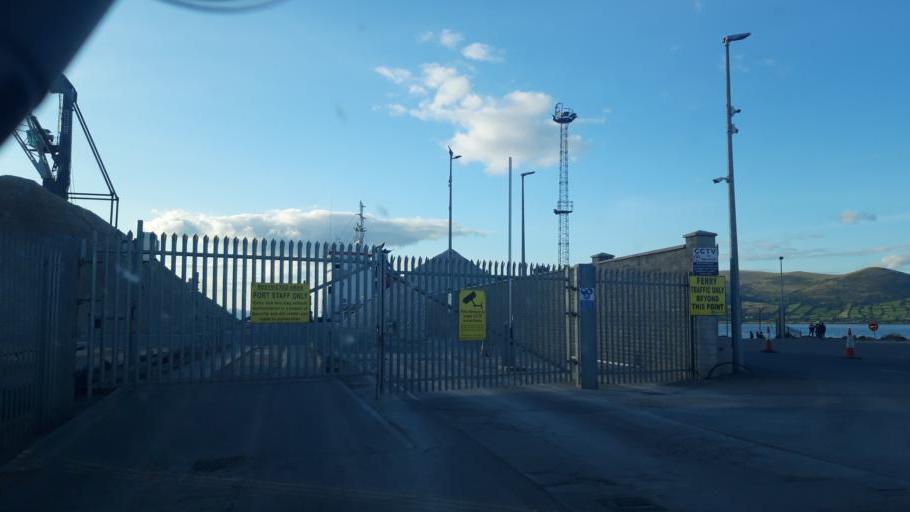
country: IE
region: Leinster
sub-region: Lu
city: Carlingford
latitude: 54.0340
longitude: -6.1319
